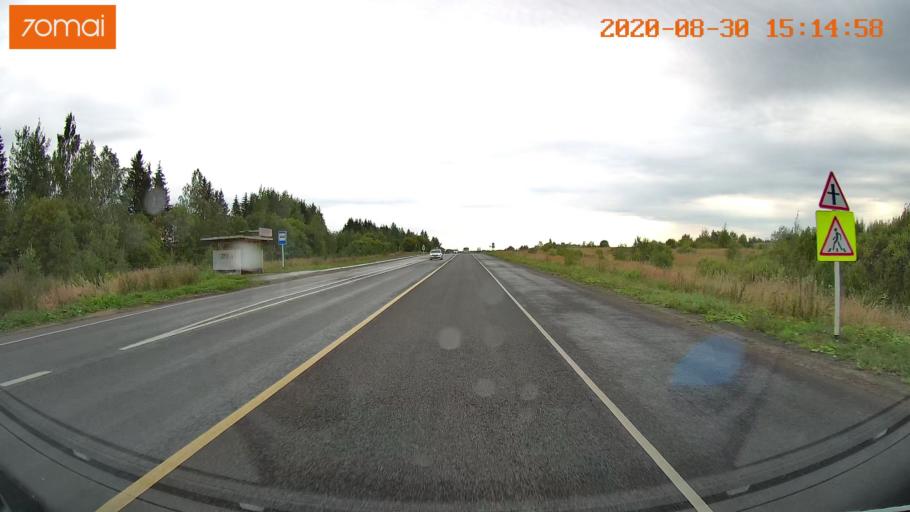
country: RU
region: Ivanovo
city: Vichuga
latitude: 57.1612
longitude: 41.8496
